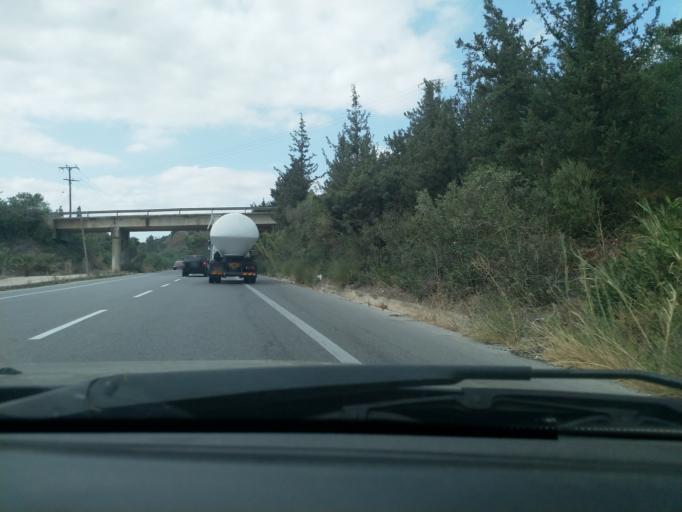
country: GR
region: Crete
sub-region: Nomos Chanias
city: Georgioupolis
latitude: 35.3758
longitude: 24.2084
